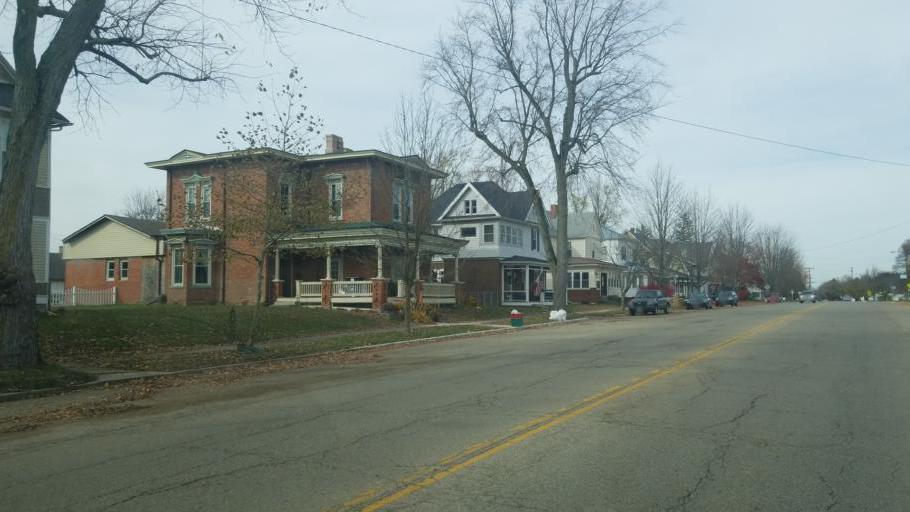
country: US
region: Ohio
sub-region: Madison County
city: London
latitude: 39.8901
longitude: -83.4527
